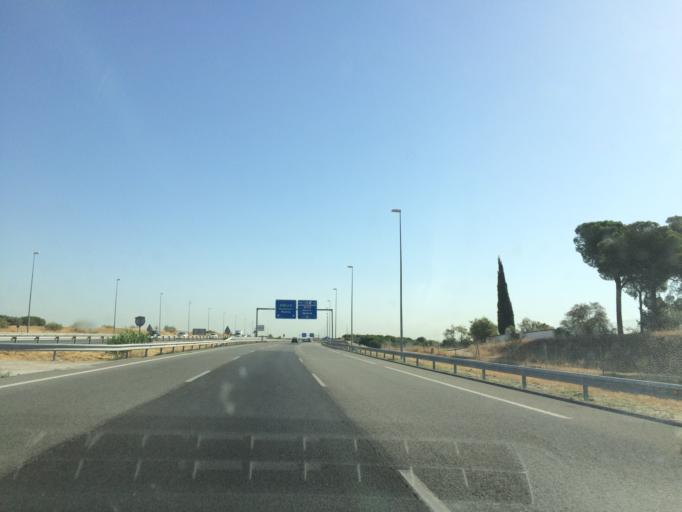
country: ES
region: Madrid
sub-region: Provincia de Madrid
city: Navalcarnero
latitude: 40.2581
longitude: -4.0464
